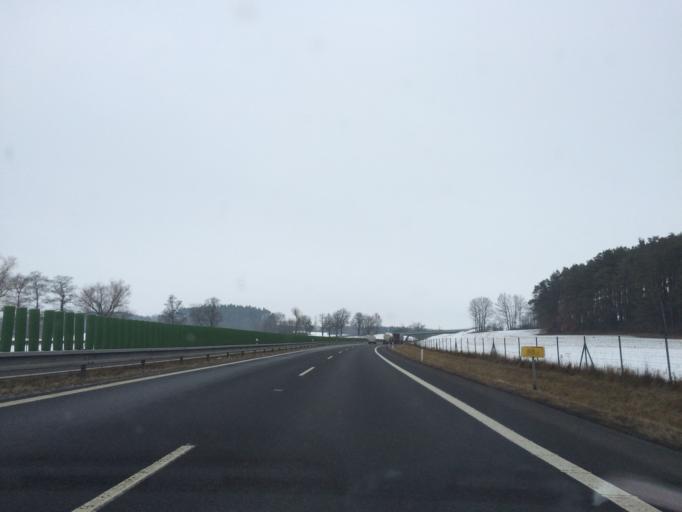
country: CZ
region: Jihocesky
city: Mirotice
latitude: 49.3940
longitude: 14.0458
